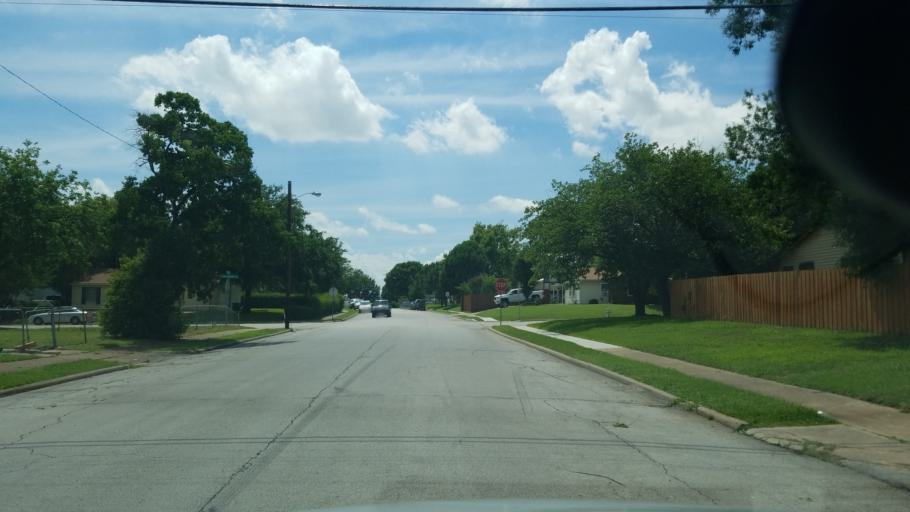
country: US
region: Texas
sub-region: Dallas County
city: Irving
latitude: 32.8511
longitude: -96.9722
